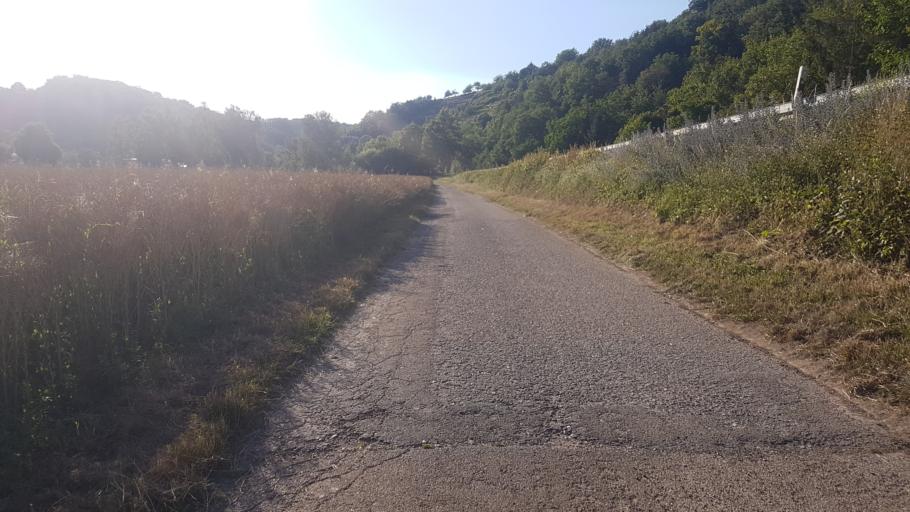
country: DE
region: Baden-Wuerttemberg
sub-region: Regierungsbezirk Stuttgart
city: Neudenau
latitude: 49.3019
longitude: 9.3151
